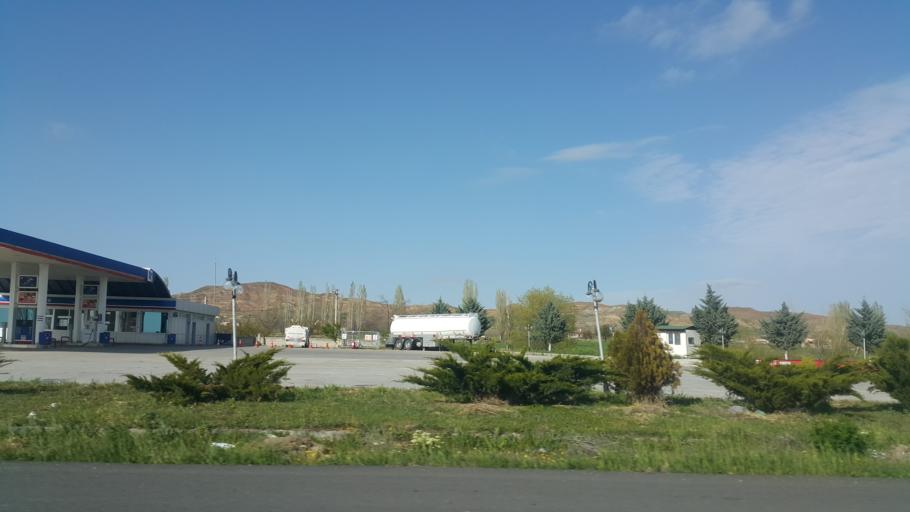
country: TR
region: Aksaray
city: Acipinar
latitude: 38.5177
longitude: 33.8494
